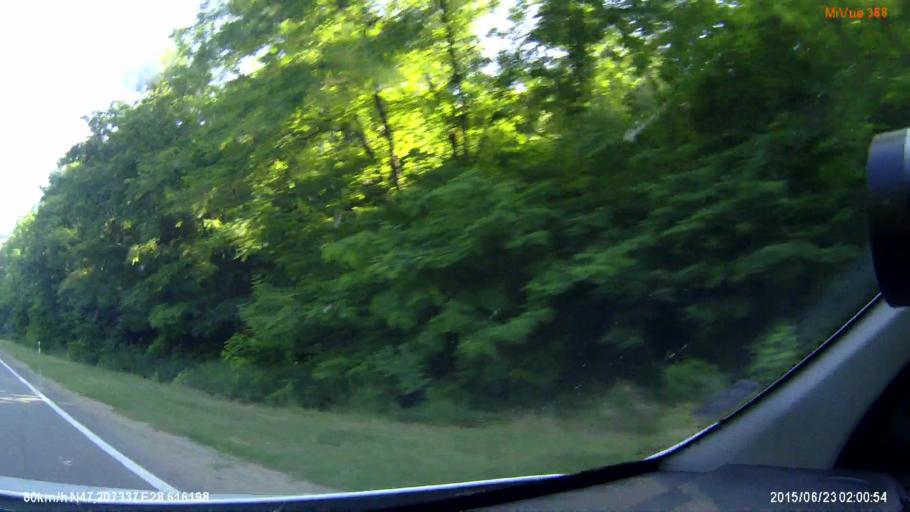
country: MD
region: Straseni
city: Straseni
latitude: 47.2077
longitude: 28.6162
